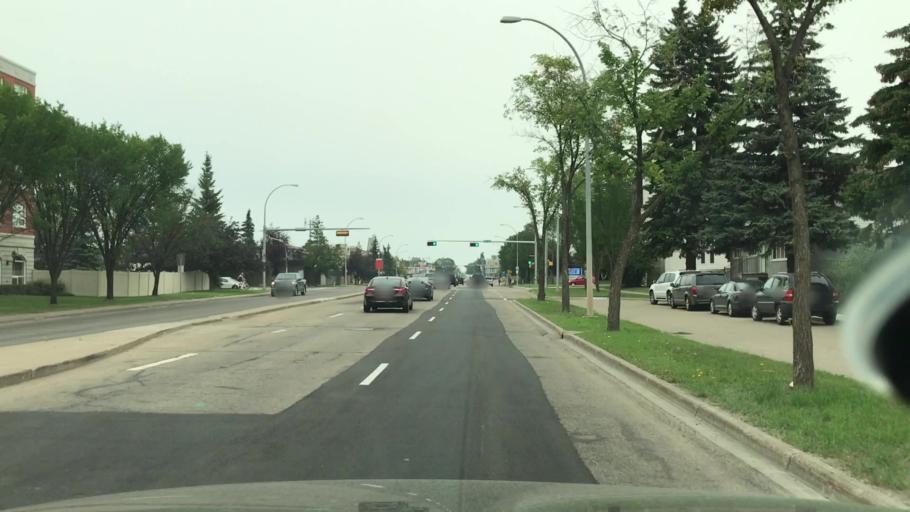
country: CA
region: Alberta
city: Edmonton
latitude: 53.5383
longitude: -113.5779
